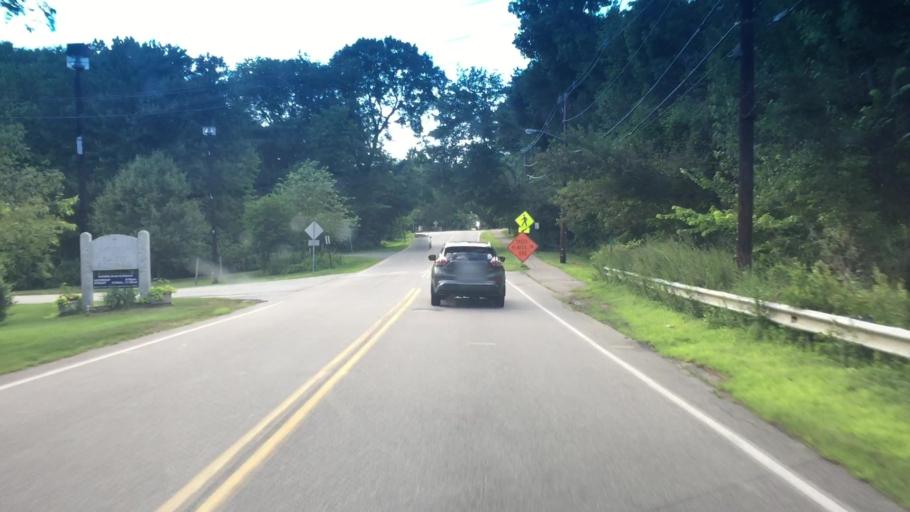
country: US
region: Massachusetts
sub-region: Norfolk County
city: Medfield
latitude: 42.1776
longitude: -71.3009
